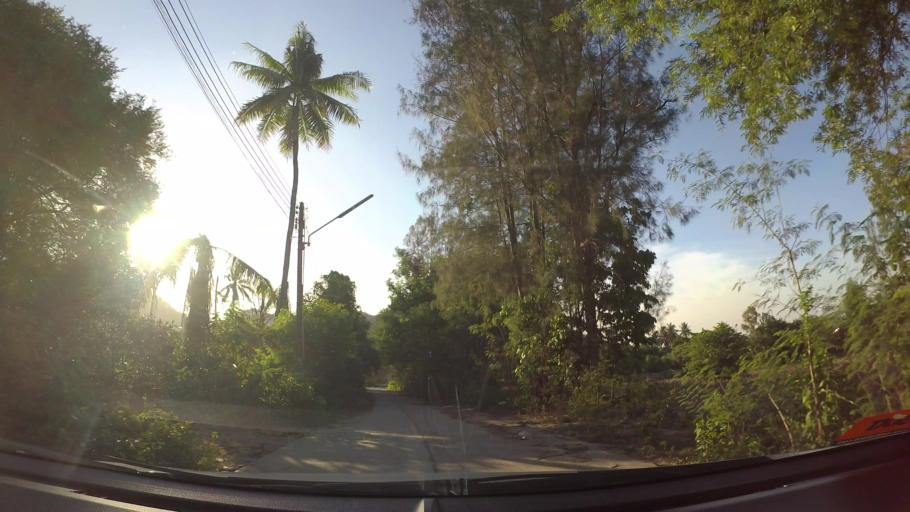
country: TH
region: Chon Buri
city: Si Racha
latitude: 13.1368
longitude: 100.9316
